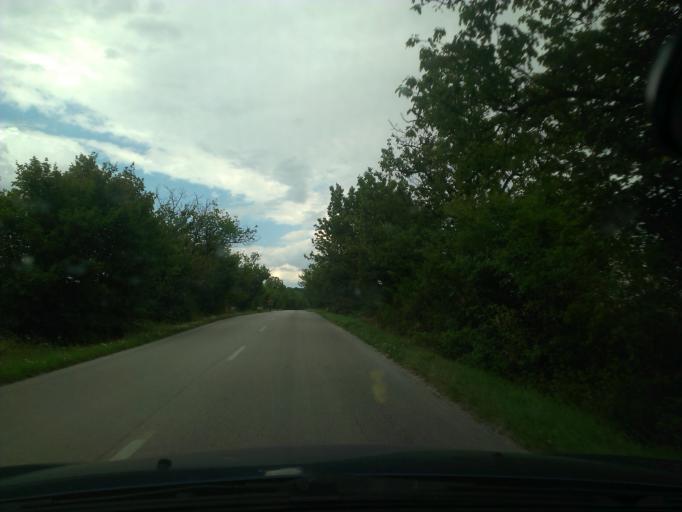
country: SK
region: Trnavsky
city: Vrbove
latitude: 48.6829
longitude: 17.6840
